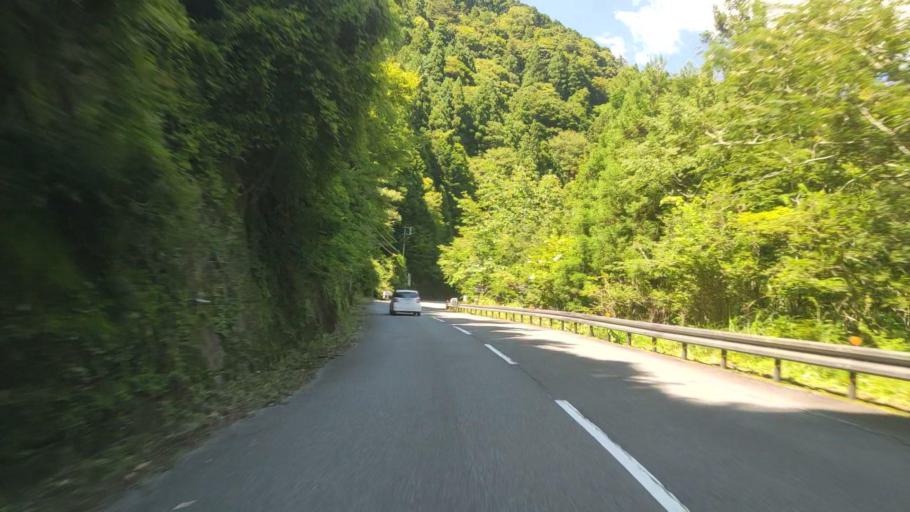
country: JP
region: Mie
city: Owase
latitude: 34.1733
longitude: 136.0023
